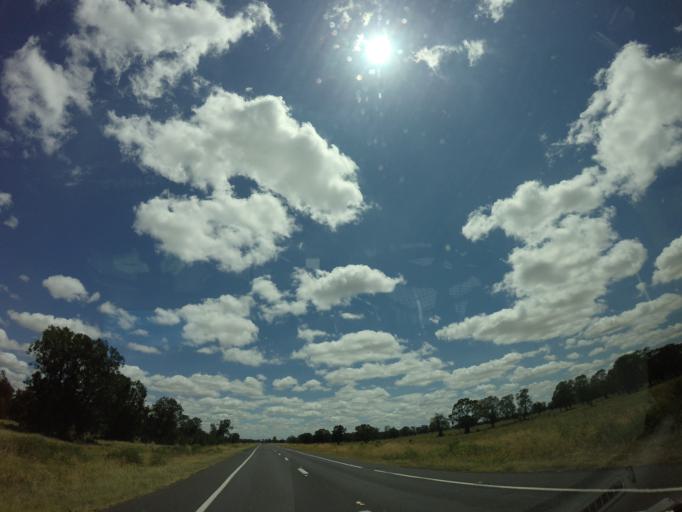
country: AU
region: New South Wales
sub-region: Moree Plains
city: Moree
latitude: -29.0892
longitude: 150.0381
